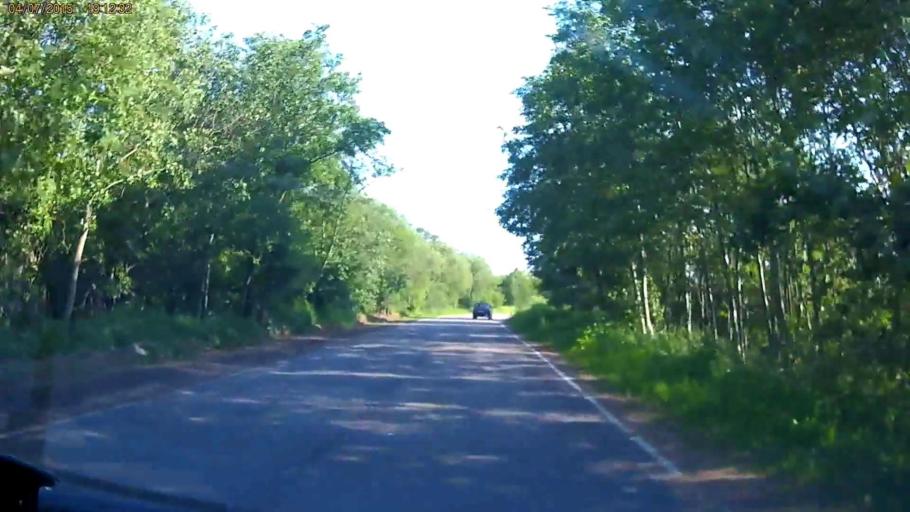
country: RU
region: Leningrad
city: Garbolovo
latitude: 60.3159
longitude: 30.4930
